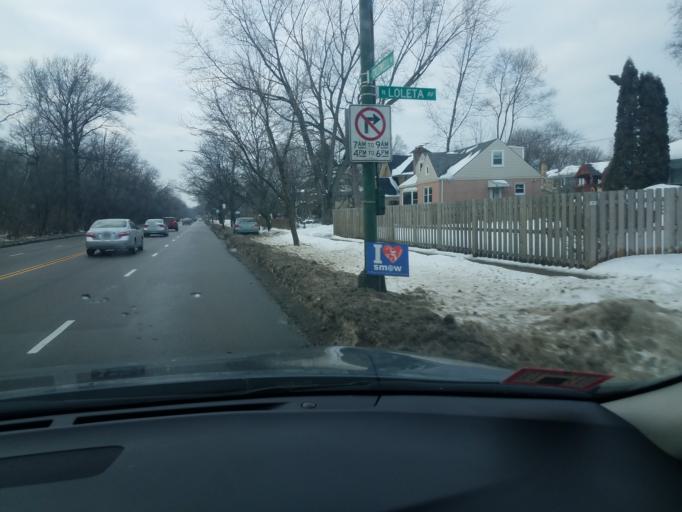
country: US
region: Illinois
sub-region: Cook County
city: Niles
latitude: 42.0007
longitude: -87.7738
